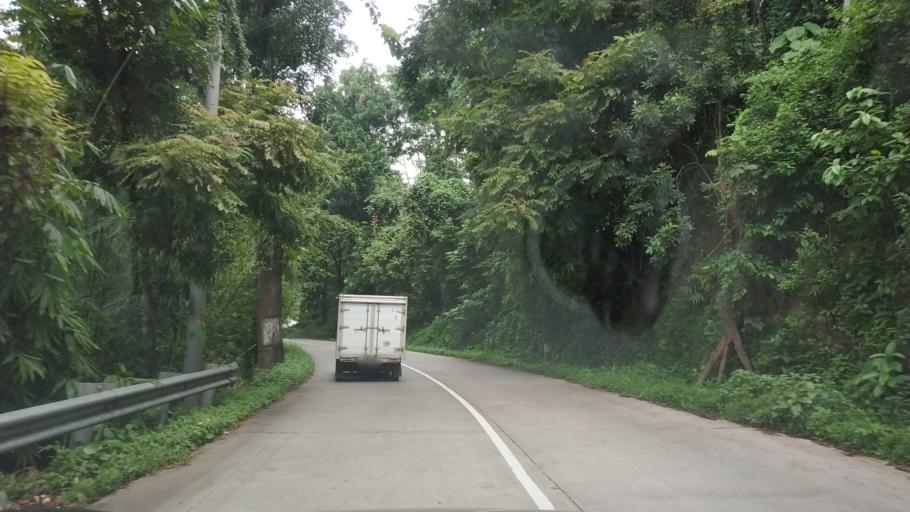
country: ID
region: Central Java
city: Weleri
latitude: -7.0025
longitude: 110.0609
